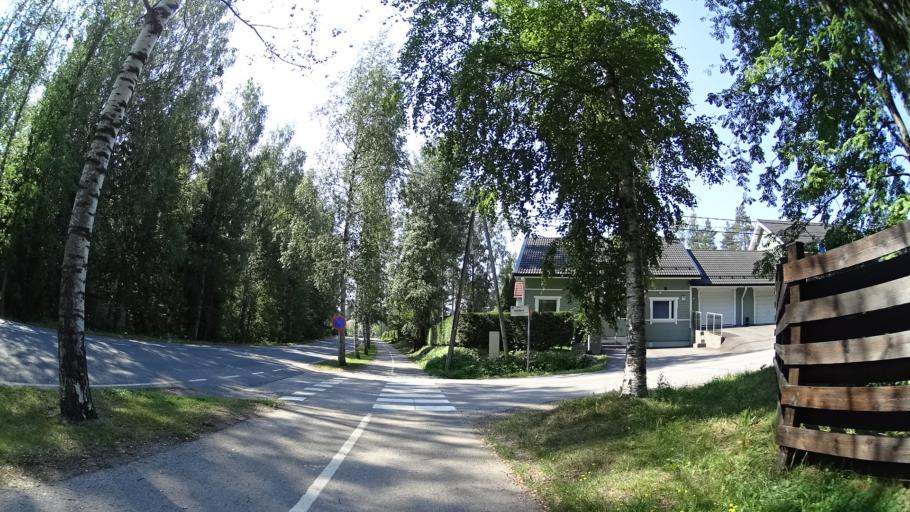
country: FI
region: Uusimaa
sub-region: Helsinki
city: Kerava
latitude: 60.3755
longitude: 25.0795
